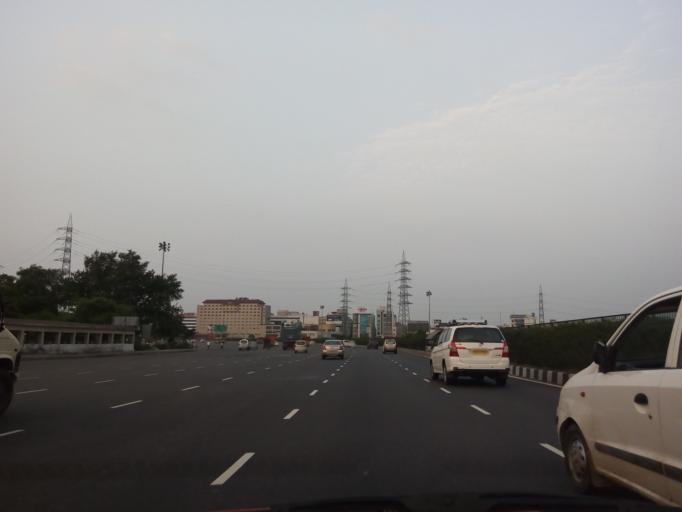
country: IN
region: Haryana
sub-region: Gurgaon
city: Gurgaon
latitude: 28.5151
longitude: 77.0939
